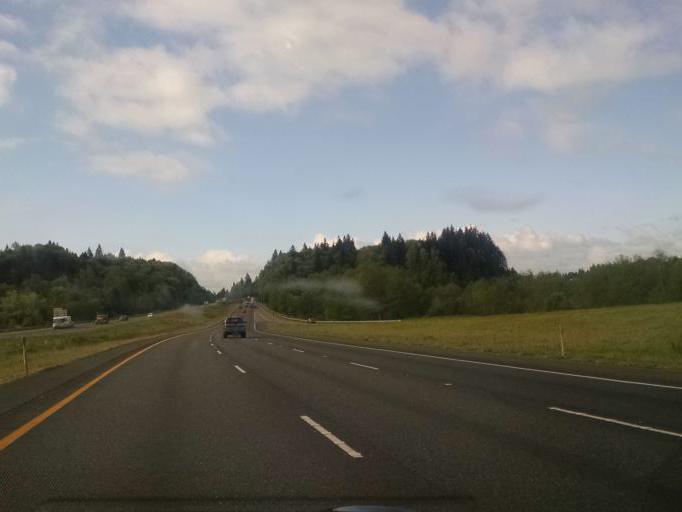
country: US
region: Washington
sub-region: Cowlitz County
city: West Side Highway
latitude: 46.1825
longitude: -122.8985
